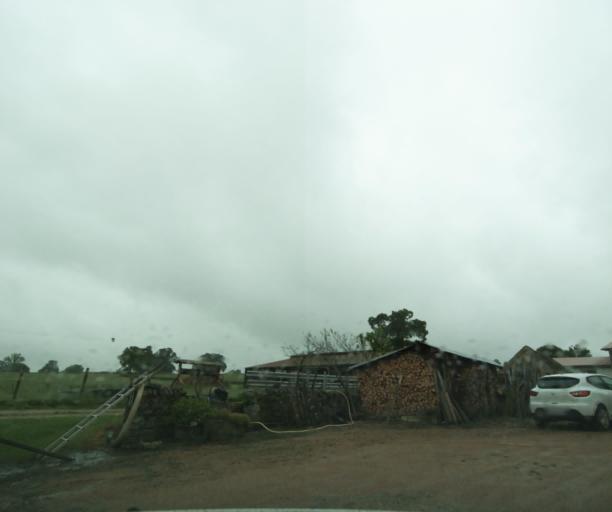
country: FR
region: Bourgogne
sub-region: Departement de Saone-et-Loire
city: Ciry-le-Noble
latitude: 46.5383
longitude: 4.3647
